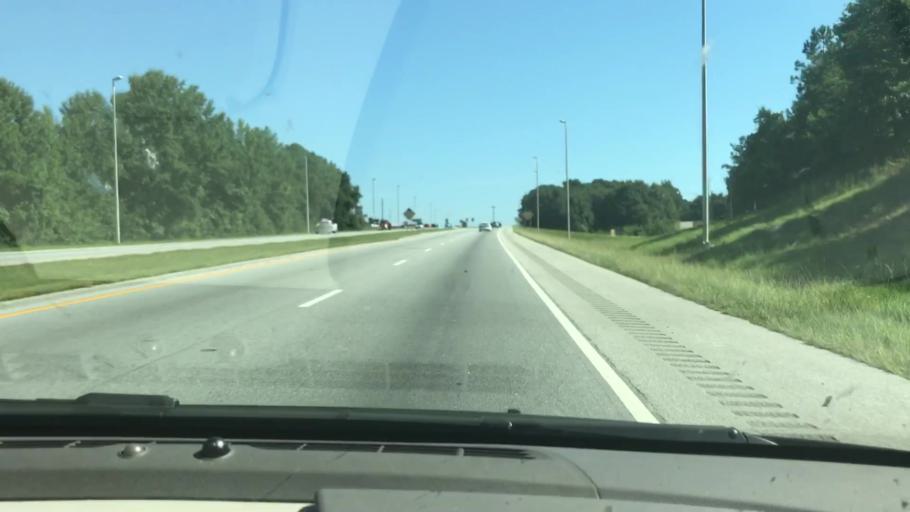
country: US
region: Alabama
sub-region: Russell County
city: Phenix City
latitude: 32.4489
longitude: -85.0161
